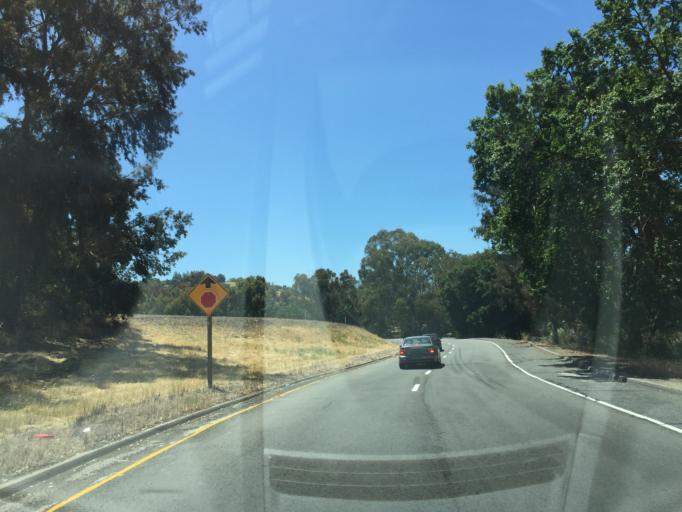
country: US
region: California
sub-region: Santa Clara County
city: Los Altos Hills
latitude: 37.3900
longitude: -122.1650
